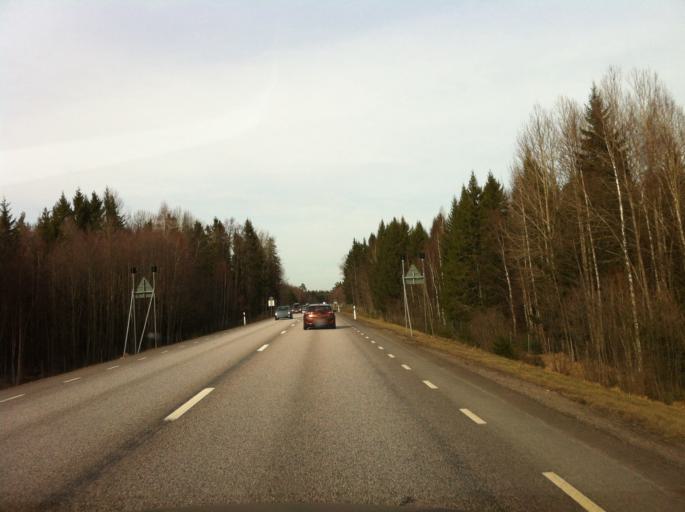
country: SE
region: Vaestra Goetaland
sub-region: Gullspangs Kommun
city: Gullspang
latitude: 58.8368
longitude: 13.9895
